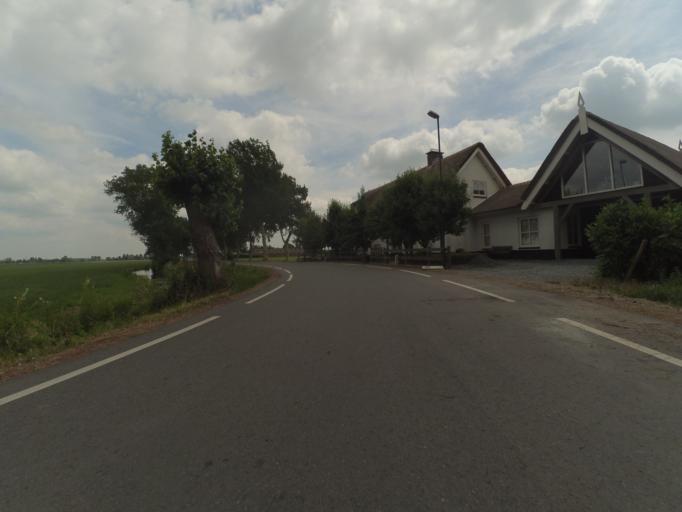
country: NL
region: South Holland
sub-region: Gemeente Gorinchem
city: Gorinchem
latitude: 51.8728
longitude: 5.0057
